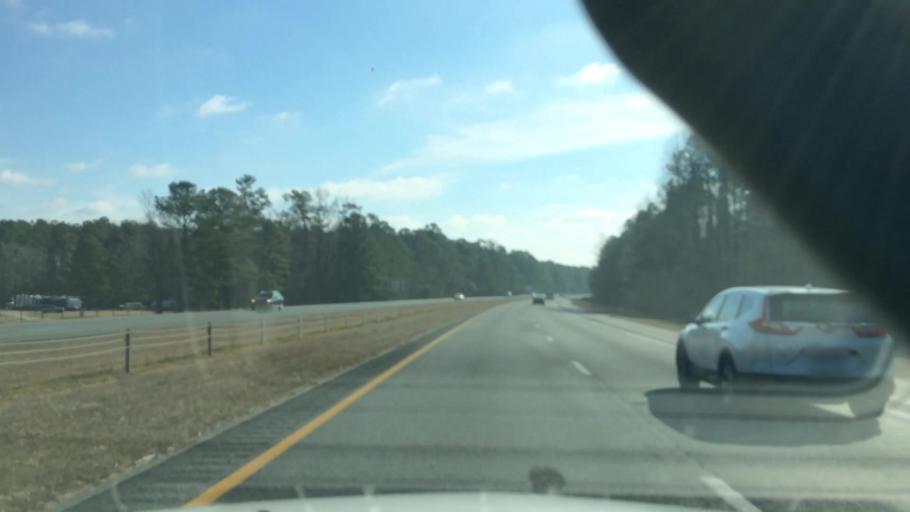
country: US
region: North Carolina
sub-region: Duplin County
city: Wallace
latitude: 34.7497
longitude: -77.9465
